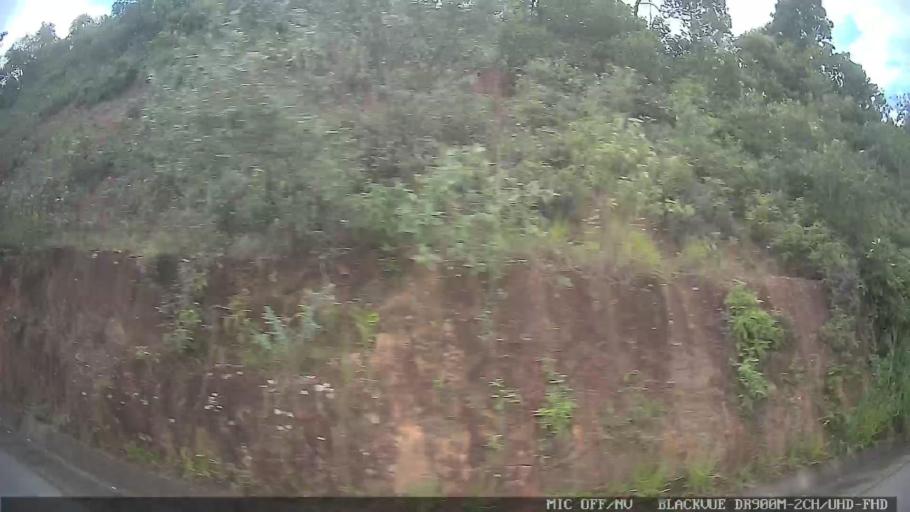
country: BR
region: Sao Paulo
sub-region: Amparo
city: Amparo
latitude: -22.7731
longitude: -46.7369
